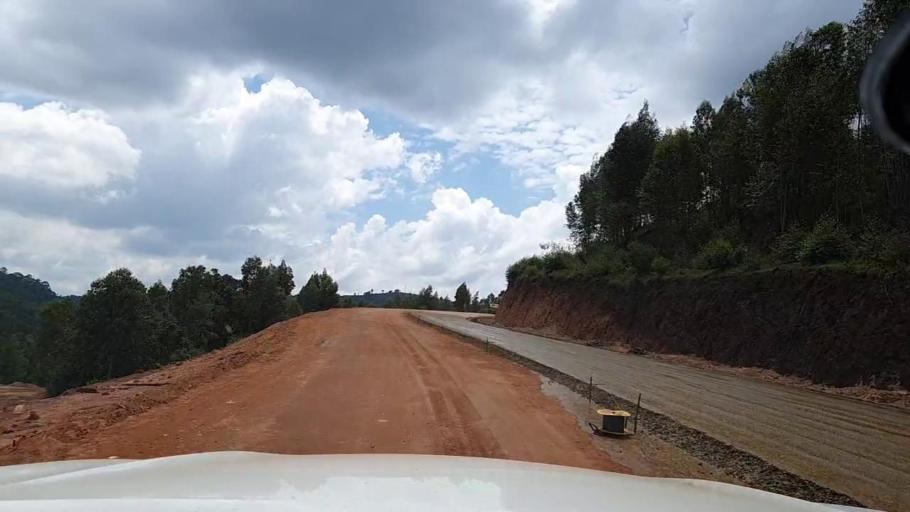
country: RW
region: Southern Province
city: Butare
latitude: -2.6986
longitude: 29.5536
